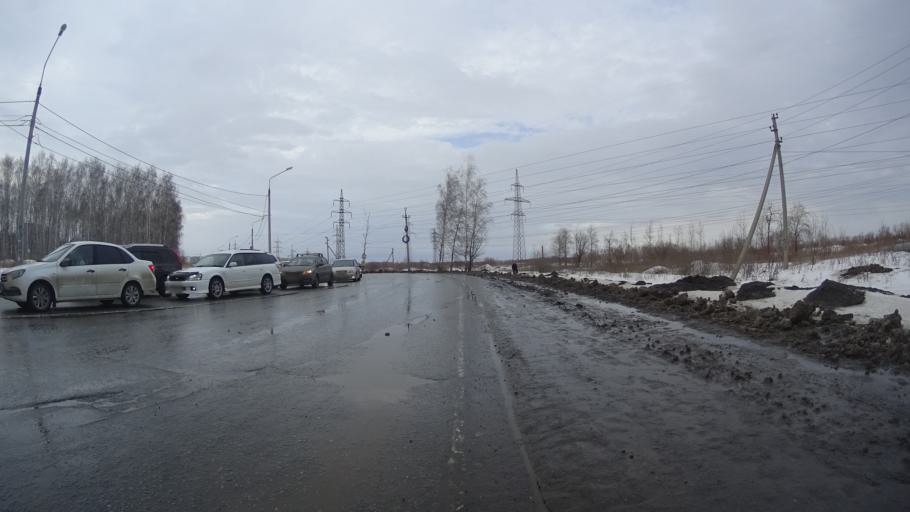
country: RU
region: Chelyabinsk
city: Roshchino
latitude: 55.2088
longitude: 61.3173
